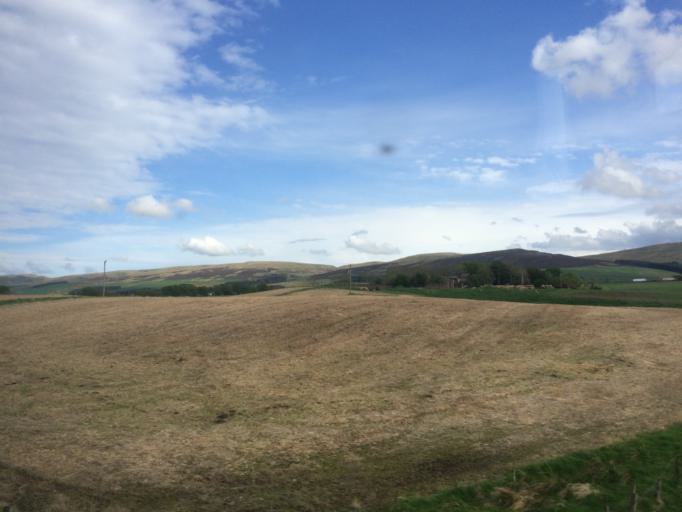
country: GB
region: Scotland
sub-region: Perth and Kinross
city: Auchterarder
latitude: 56.2637
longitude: -3.8039
